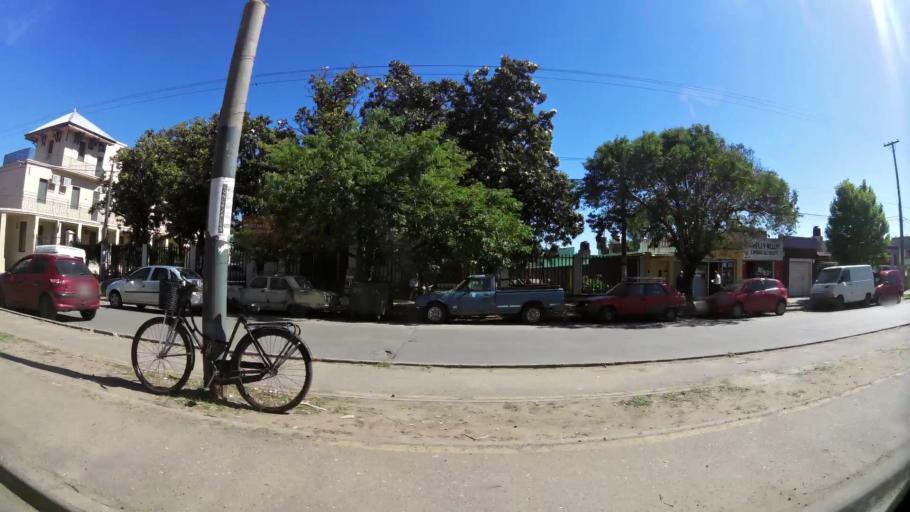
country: AR
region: Santa Fe
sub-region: Departamento de Rosario
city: Rosario
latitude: -32.9706
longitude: -60.6959
